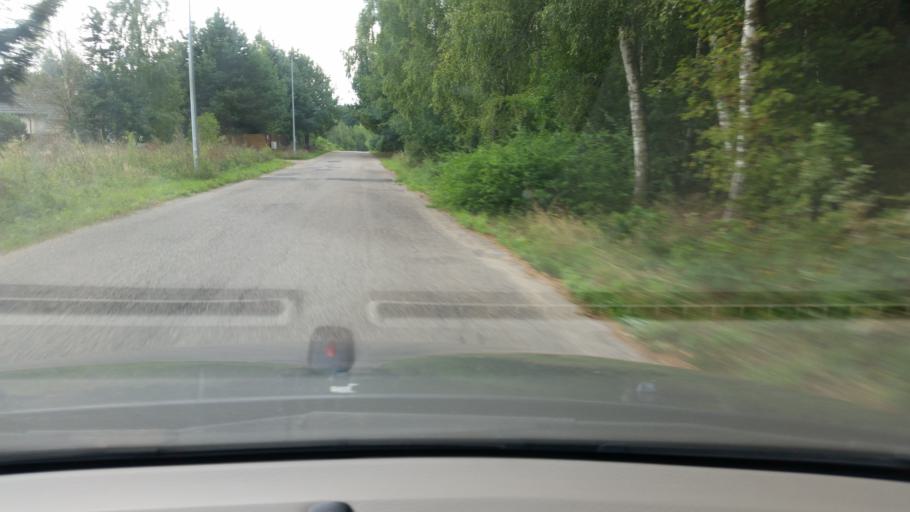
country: PL
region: Pomeranian Voivodeship
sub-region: Powiat wejherowski
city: Choczewo
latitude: 54.7648
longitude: 17.7929
